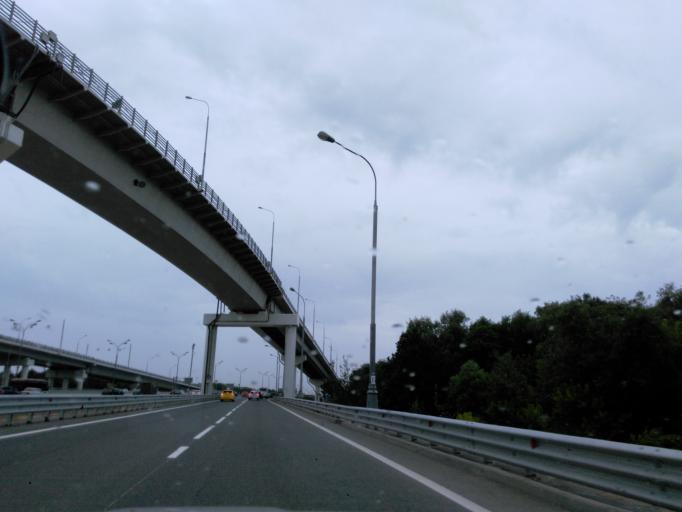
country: RU
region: Moskovskaya
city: Levoberezhnaya
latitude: 55.8867
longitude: 37.4785
